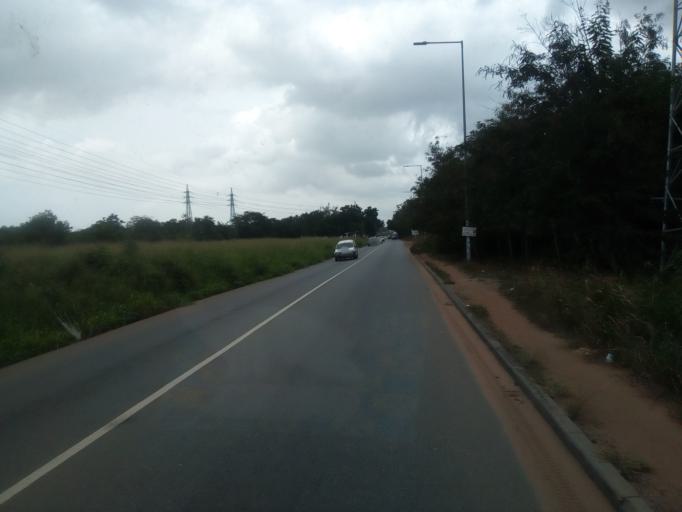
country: GH
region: Greater Accra
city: Dome
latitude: 5.6424
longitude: -0.2037
